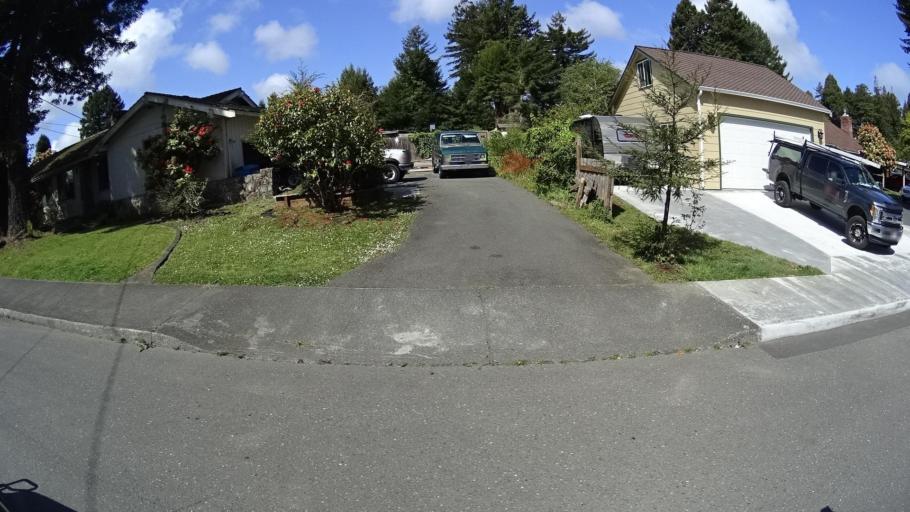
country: US
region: California
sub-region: Humboldt County
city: Cutten
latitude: 40.7774
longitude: -124.1397
